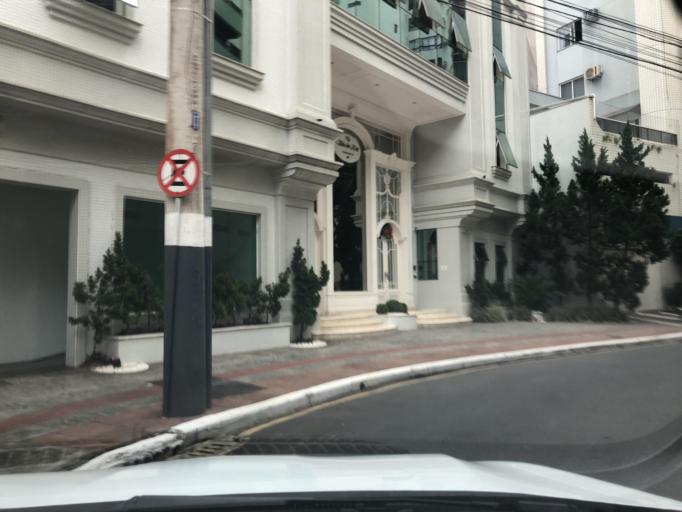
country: BR
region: Santa Catarina
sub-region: Balneario Camboriu
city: Balneario Camboriu
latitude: -26.9999
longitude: -48.6236
